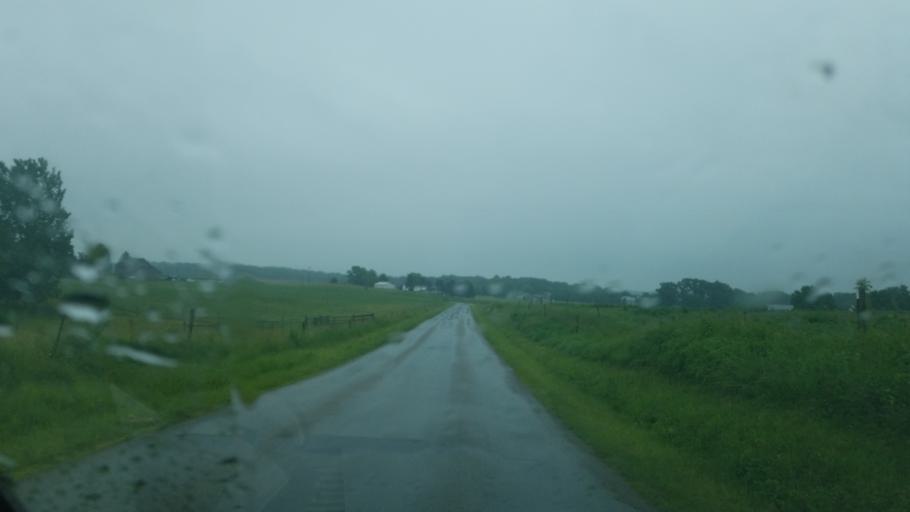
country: US
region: Ohio
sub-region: Huron County
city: Plymouth
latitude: 40.9769
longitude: -82.5876
